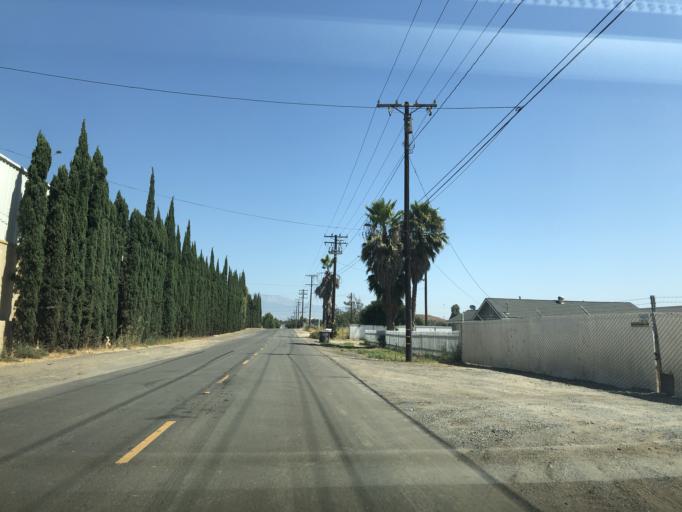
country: US
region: California
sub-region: Riverside County
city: Norco
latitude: 33.9062
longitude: -117.5669
